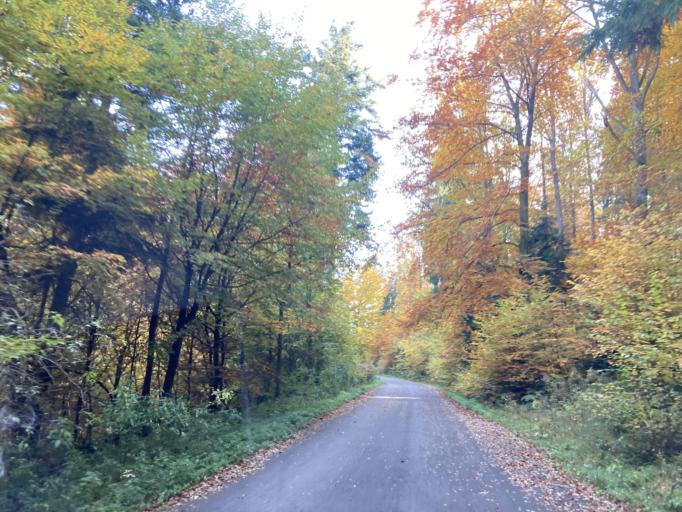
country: DE
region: Baden-Wuerttemberg
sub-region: Tuebingen Region
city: Rottenburg
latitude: 48.4271
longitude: 8.9439
